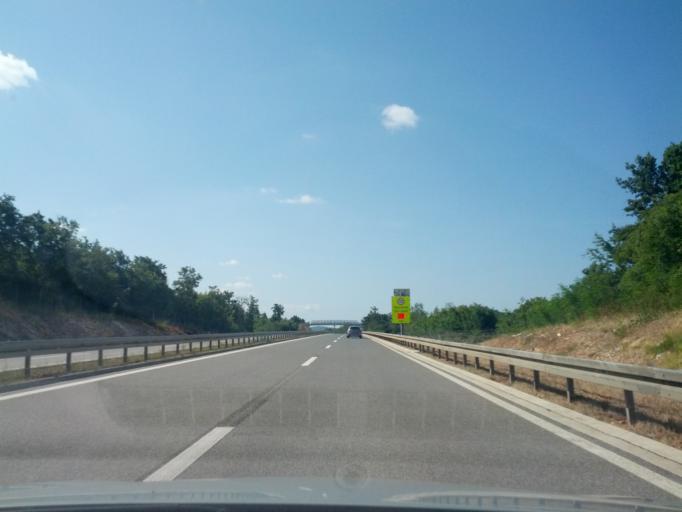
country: HR
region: Istarska
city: Vrsar
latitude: 45.1943
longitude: 13.7303
